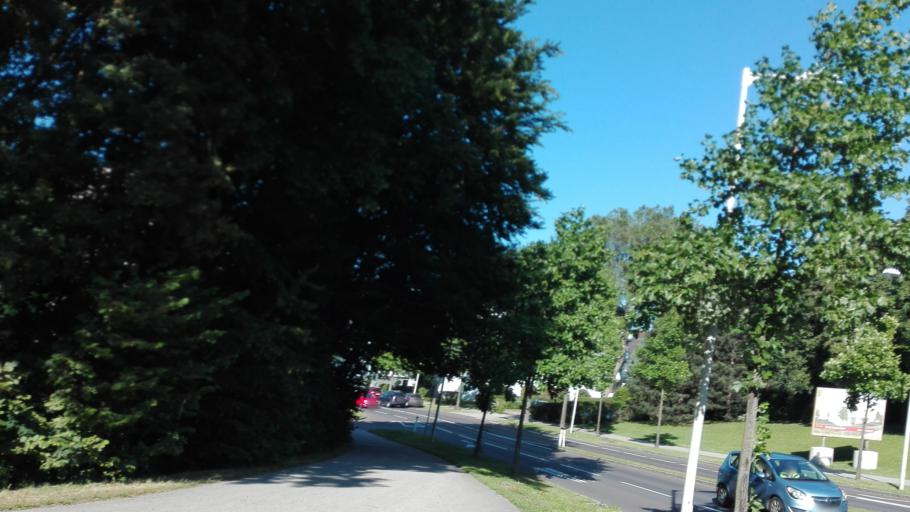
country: AT
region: Upper Austria
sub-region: Linz Stadt
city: Linz
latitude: 48.2723
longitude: 14.2966
